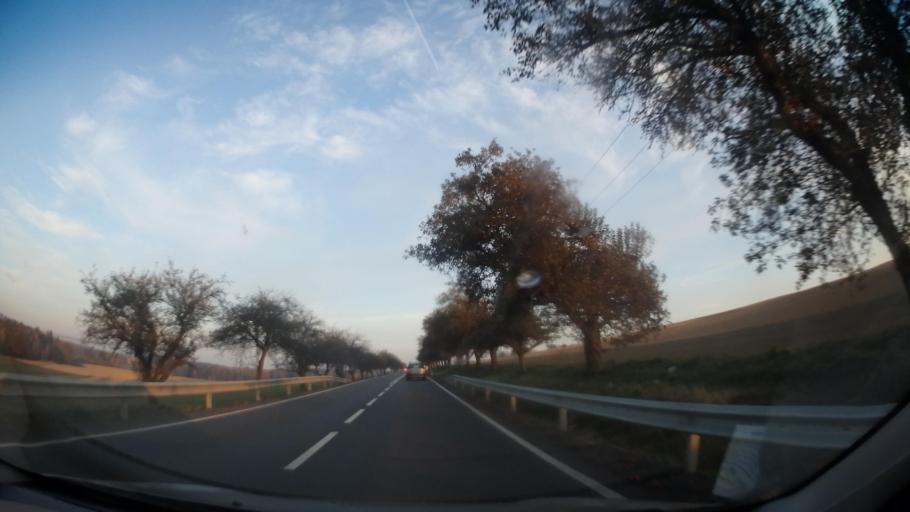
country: CZ
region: Central Bohemia
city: Trhovy Stepanov
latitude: 49.6621
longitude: 14.9922
